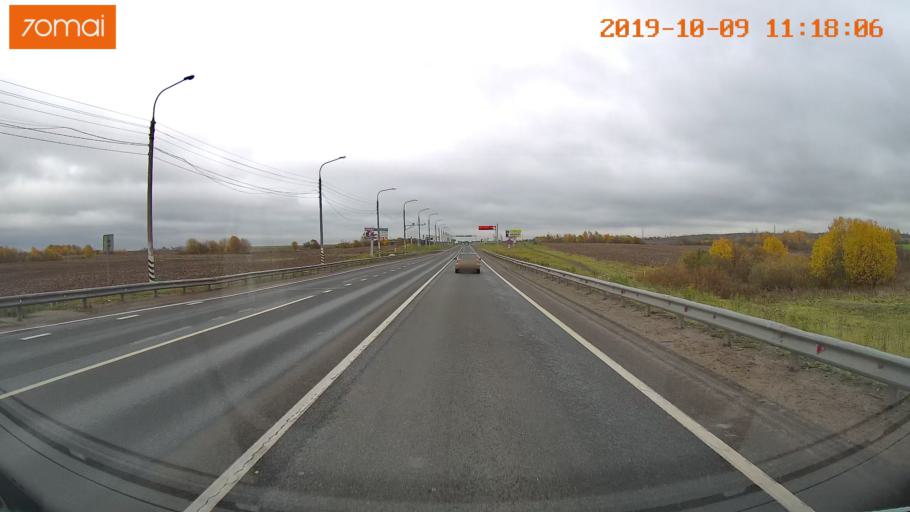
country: RU
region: Vologda
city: Vologda
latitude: 59.1705
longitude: 39.9095
